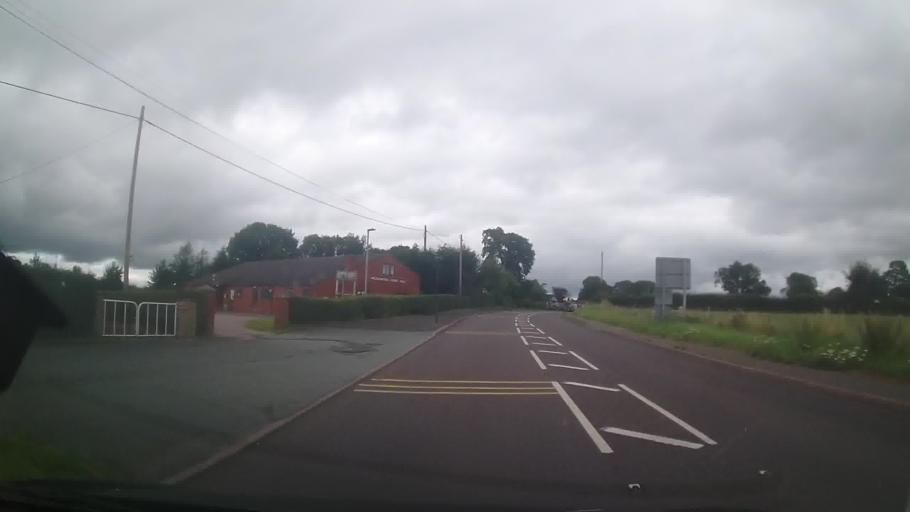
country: GB
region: England
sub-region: Shropshire
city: Ellesmere
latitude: 52.9105
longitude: -2.8380
